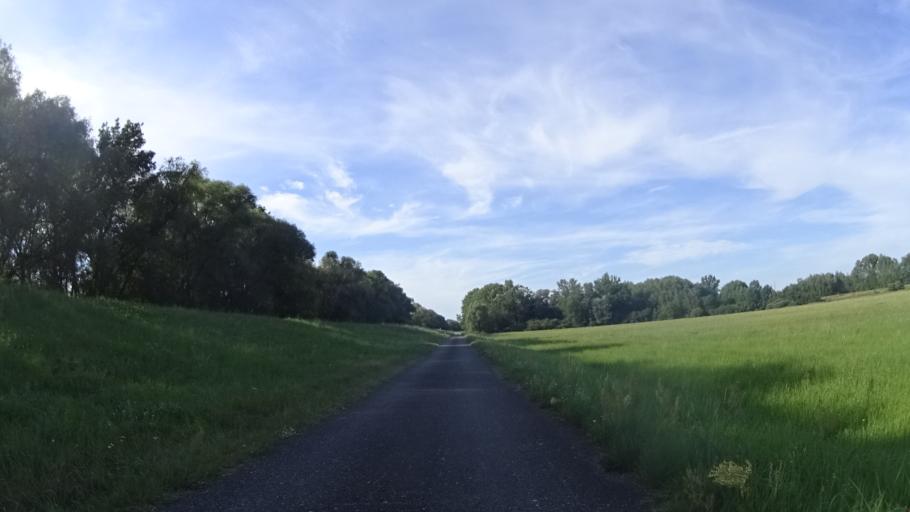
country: AT
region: Lower Austria
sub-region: Politischer Bezirk Ganserndorf
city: Drosing
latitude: 48.5507
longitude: 16.9624
